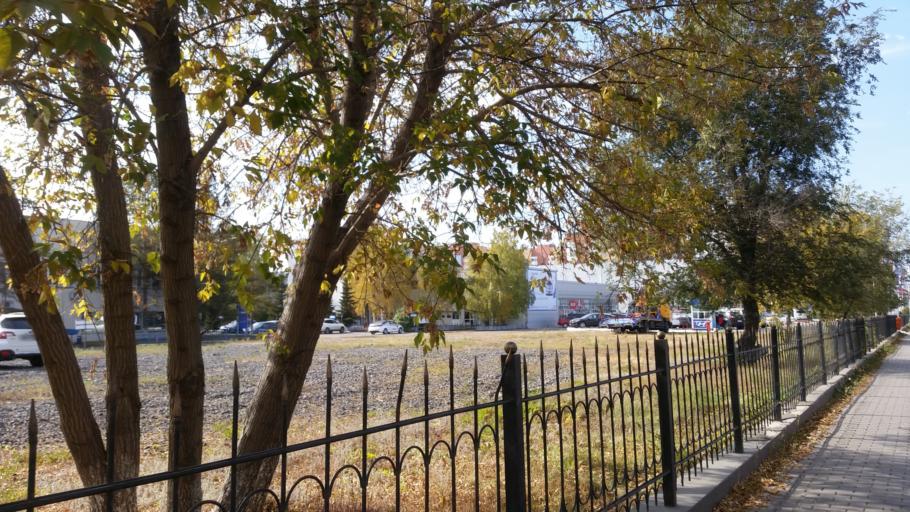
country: KZ
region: Astana Qalasy
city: Astana
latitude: 51.1625
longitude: 71.4828
